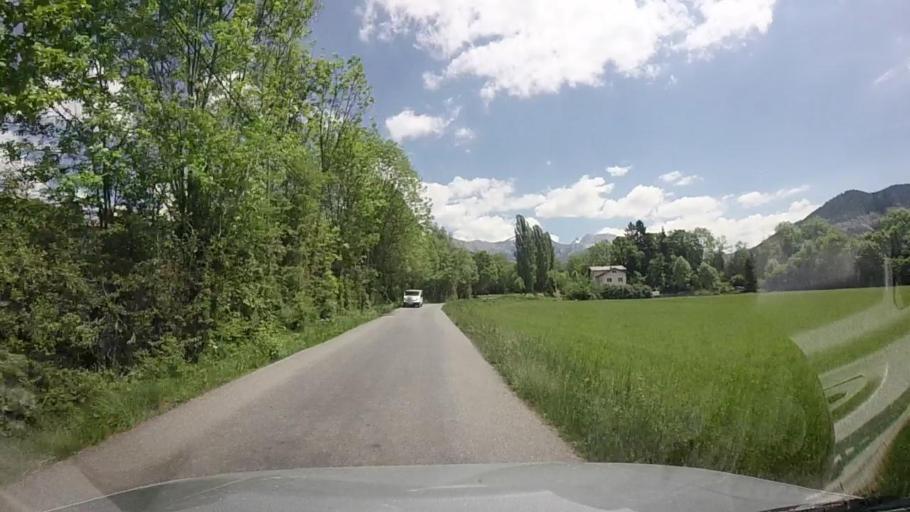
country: FR
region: Provence-Alpes-Cote d'Azur
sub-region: Departement des Alpes-de-Haute-Provence
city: Seyne-les-Alpes
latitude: 44.3482
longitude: 6.3546
